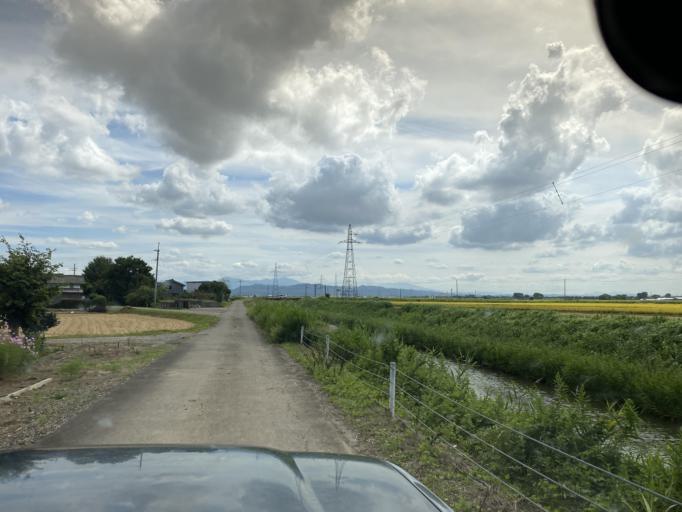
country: JP
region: Niigata
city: Niitsu-honcho
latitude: 37.8189
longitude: 139.0772
